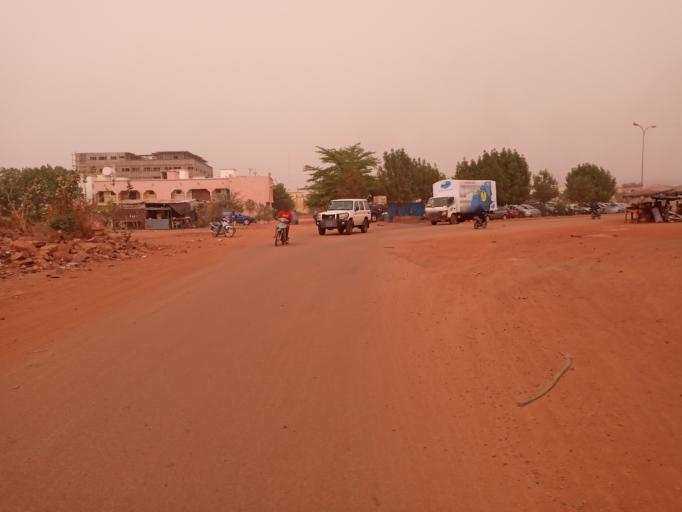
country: ML
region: Bamako
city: Bamako
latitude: 12.6527
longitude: -7.9353
